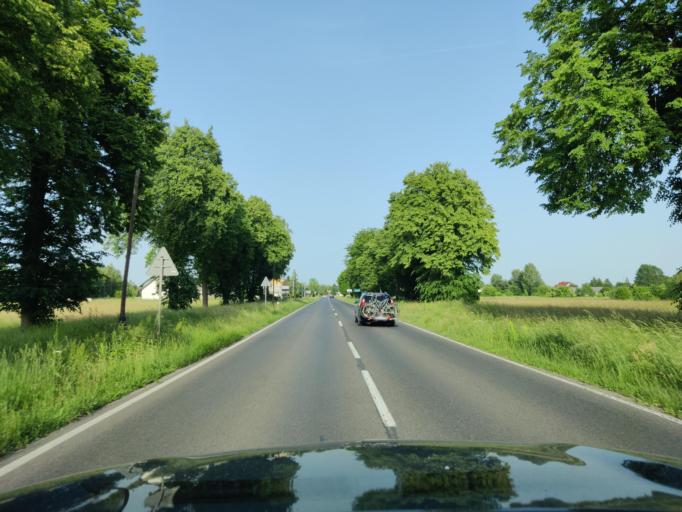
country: PL
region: Masovian Voivodeship
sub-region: Powiat wegrowski
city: Lochow
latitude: 52.5402
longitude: 21.6562
